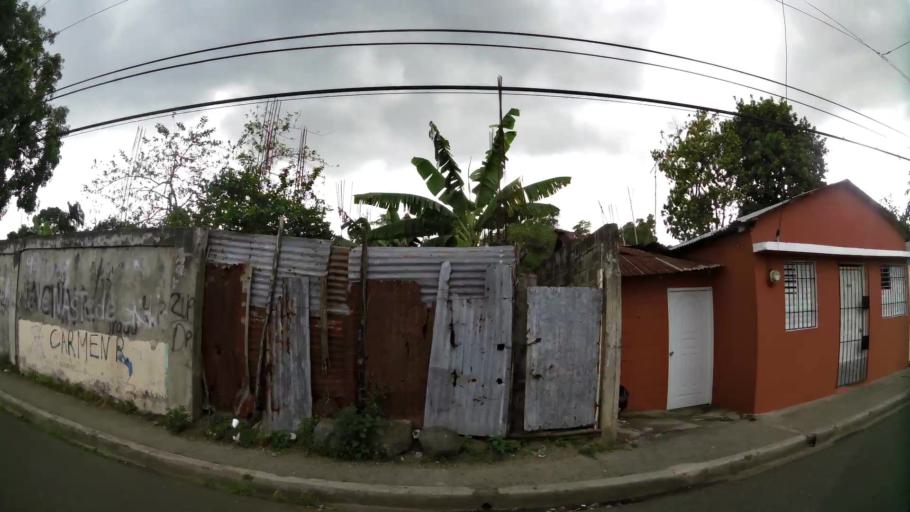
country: DO
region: Monsenor Nouel
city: Bonao
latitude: 18.9486
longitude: -70.4068
